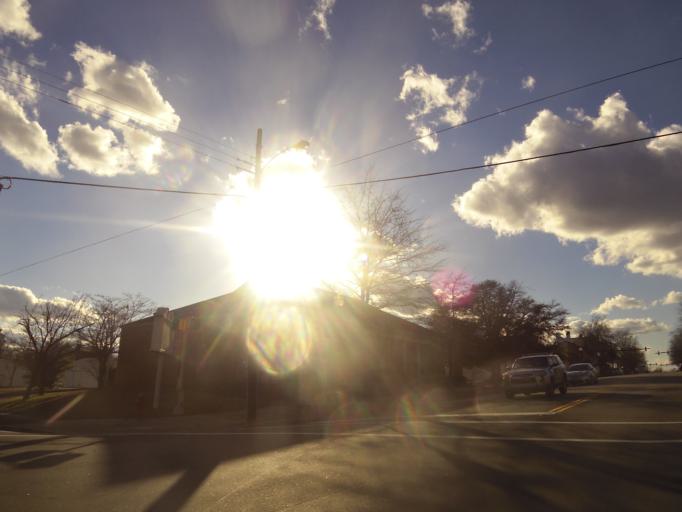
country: US
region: South Carolina
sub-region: Clarendon County
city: Manning
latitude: 33.6953
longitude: -80.2092
